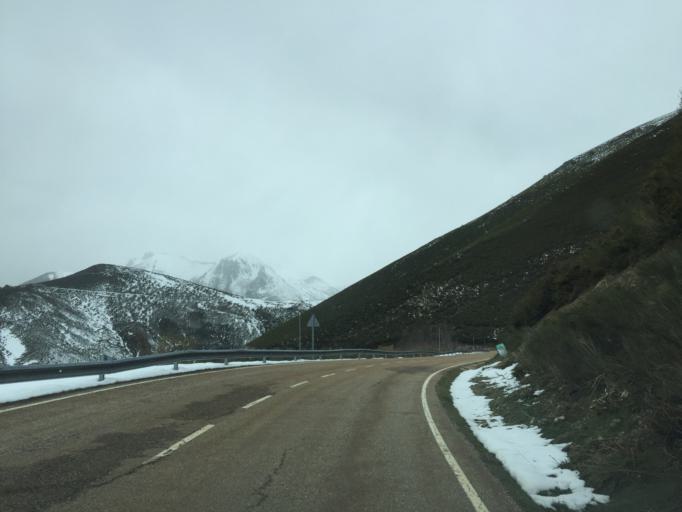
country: ES
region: Castille and Leon
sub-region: Provincia de Leon
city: San Emiliano
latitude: 43.0529
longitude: -6.0095
